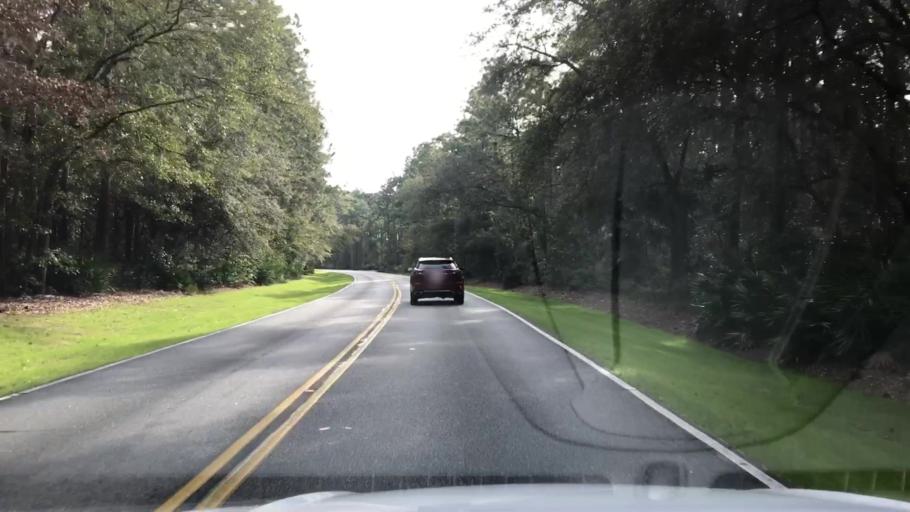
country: US
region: South Carolina
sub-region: Beaufort County
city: Hilton Head Island
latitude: 32.2329
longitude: -80.7251
